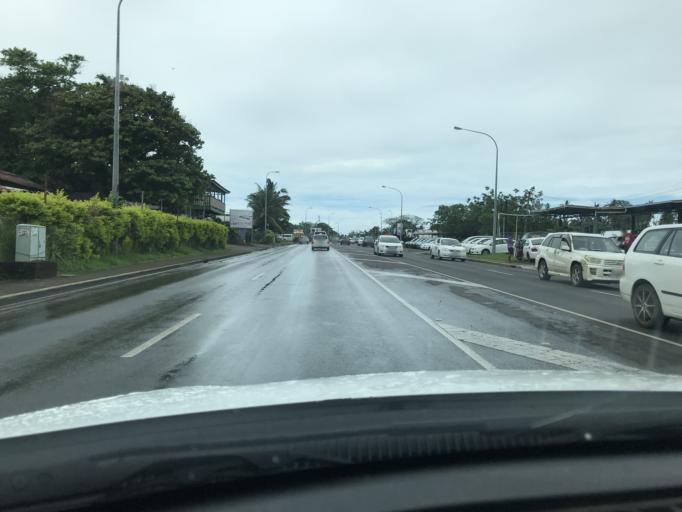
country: WS
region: Tuamasaga
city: Vaiusu
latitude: -13.8368
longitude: -171.7846
